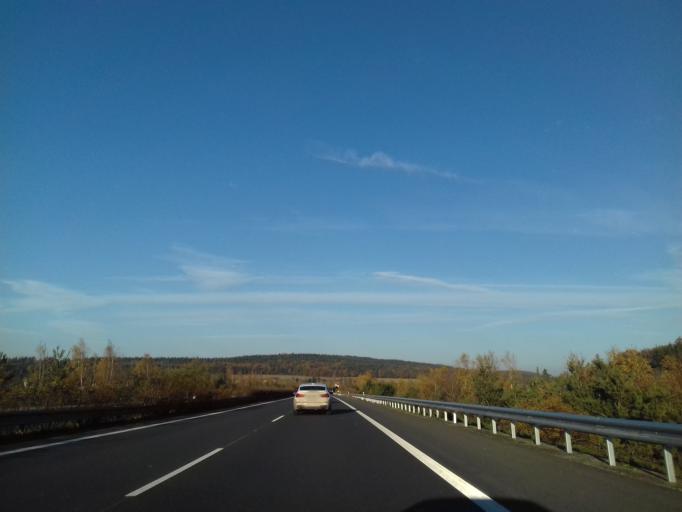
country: CZ
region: Plzensky
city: Zbiroh
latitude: 49.8275
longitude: 13.7779
